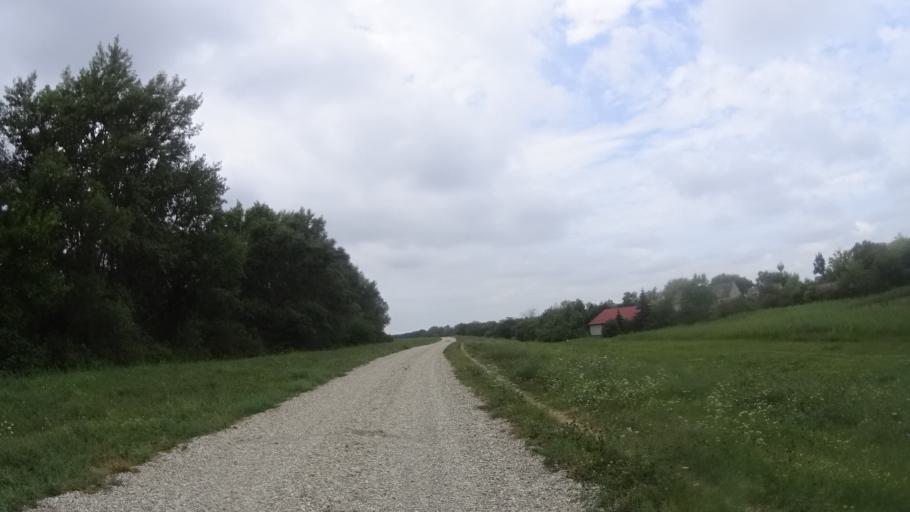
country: HU
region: Komarom-Esztergom
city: Acs
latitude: 47.7555
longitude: 17.9463
